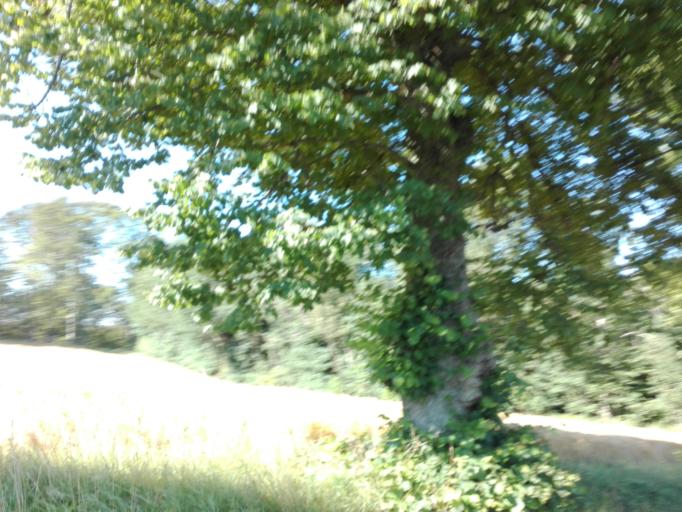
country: DK
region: Central Jutland
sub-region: Odder Kommune
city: Odder
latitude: 55.9619
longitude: 10.1195
